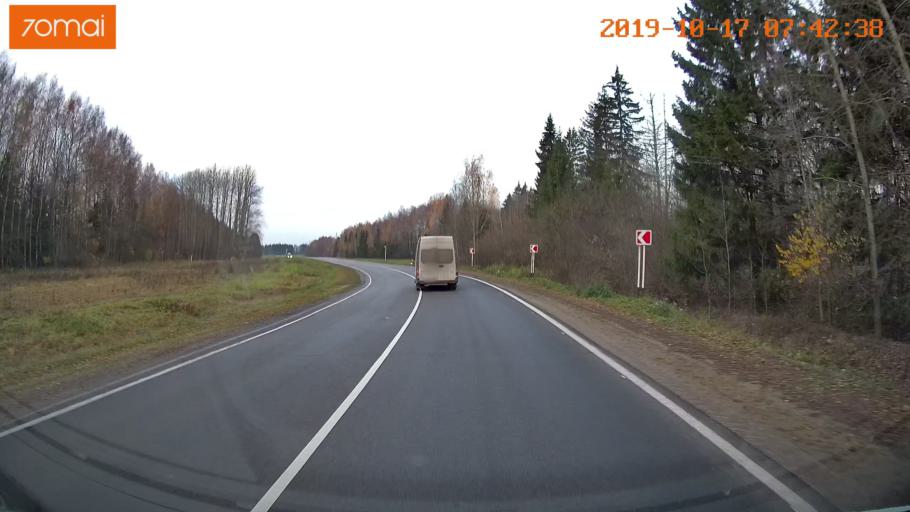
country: RU
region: Vladimir
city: Yur'yev-Pol'skiy
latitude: 56.4846
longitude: 39.7834
